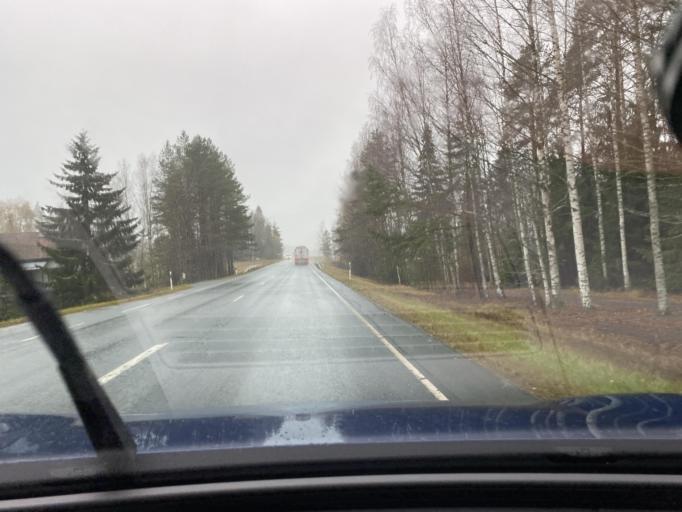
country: FI
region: Haeme
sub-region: Forssa
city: Jokioinen
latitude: 60.7789
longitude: 23.4045
